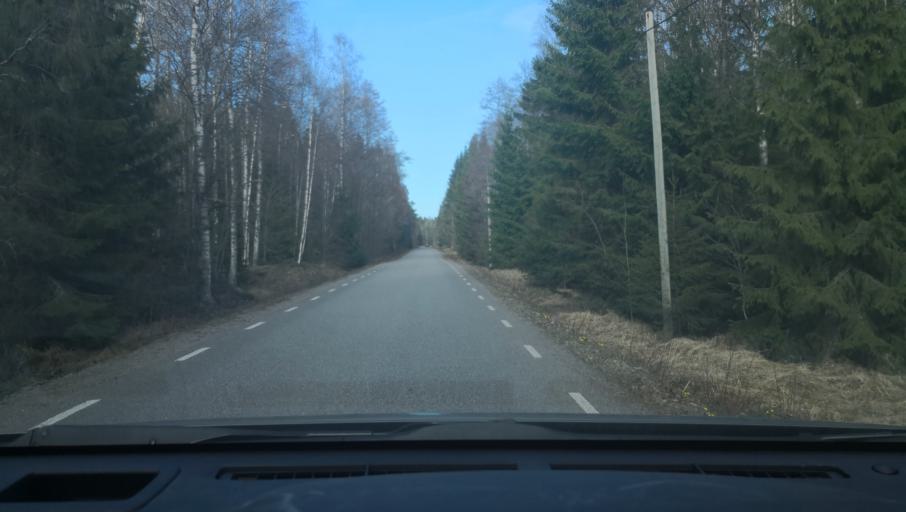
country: SE
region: Uppsala
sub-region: Heby Kommun
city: Heby
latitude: 59.9047
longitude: 16.8150
